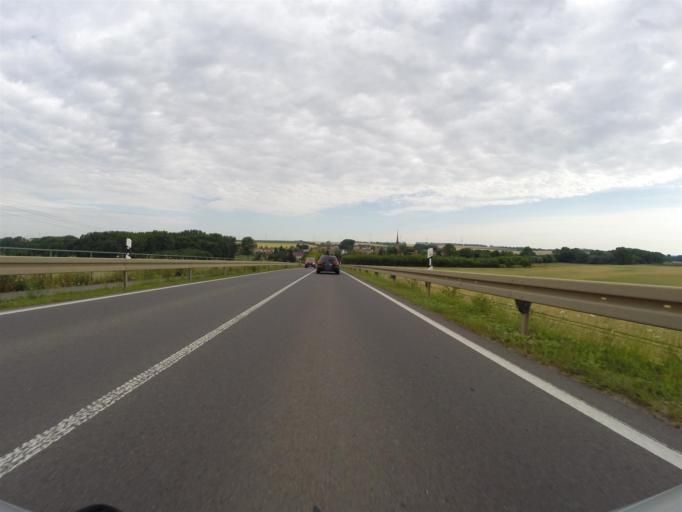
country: DE
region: Thuringia
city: Berlstedt
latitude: 51.0737
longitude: 11.2444
